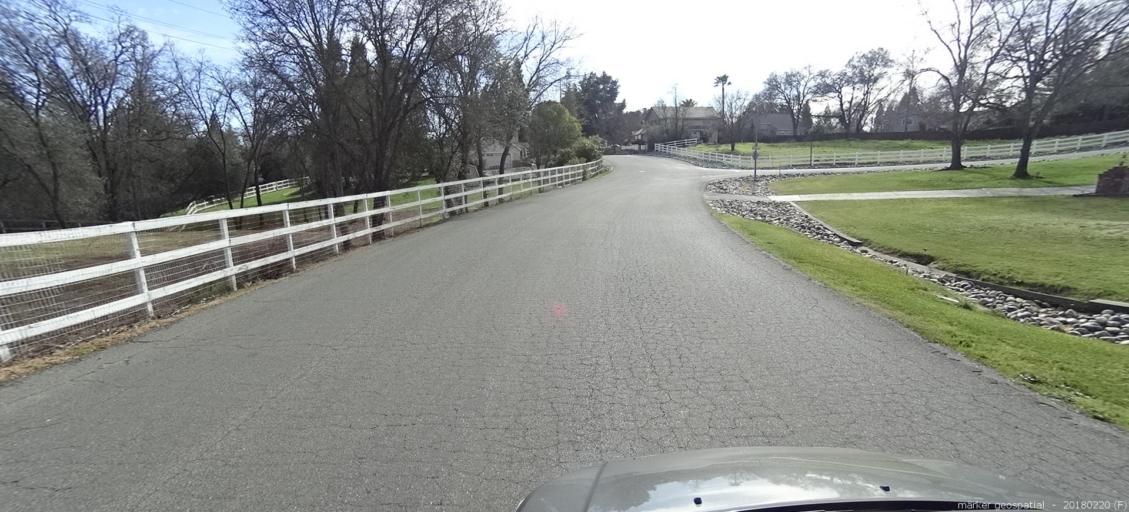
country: US
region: California
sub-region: Sacramento County
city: Orangevale
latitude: 38.7100
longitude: -121.2388
